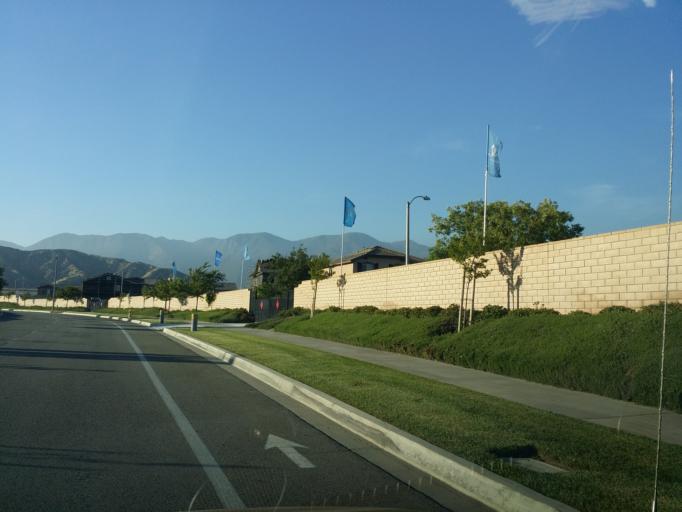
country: US
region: California
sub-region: San Bernardino County
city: Muscoy
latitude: 34.1896
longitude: -117.4175
